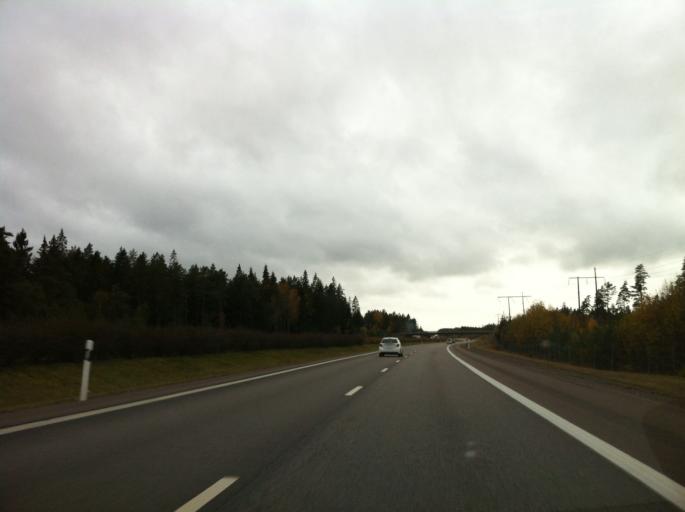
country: SE
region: OEstergoetland
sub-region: Vadstena Kommun
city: Herrestad
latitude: 58.2526
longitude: 14.8110
